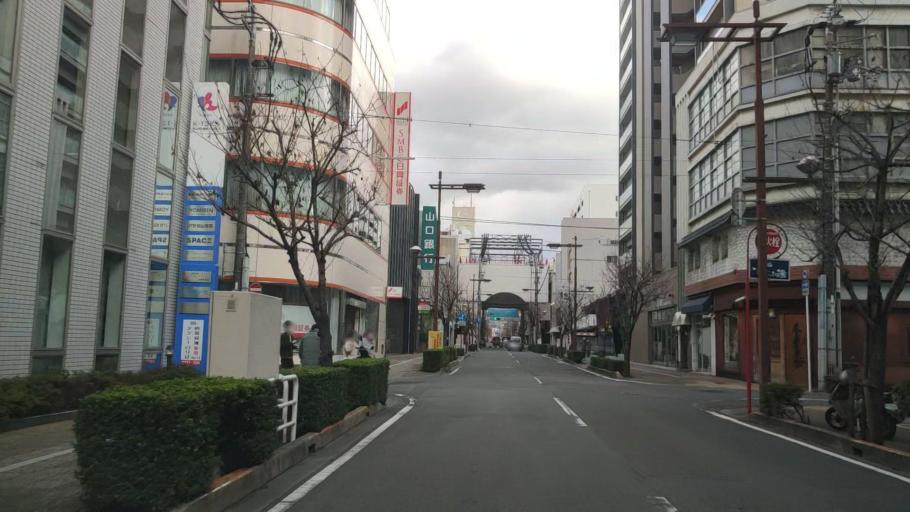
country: JP
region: Ehime
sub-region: Shikoku-chuo Shi
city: Matsuyama
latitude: 33.8383
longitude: 132.7688
